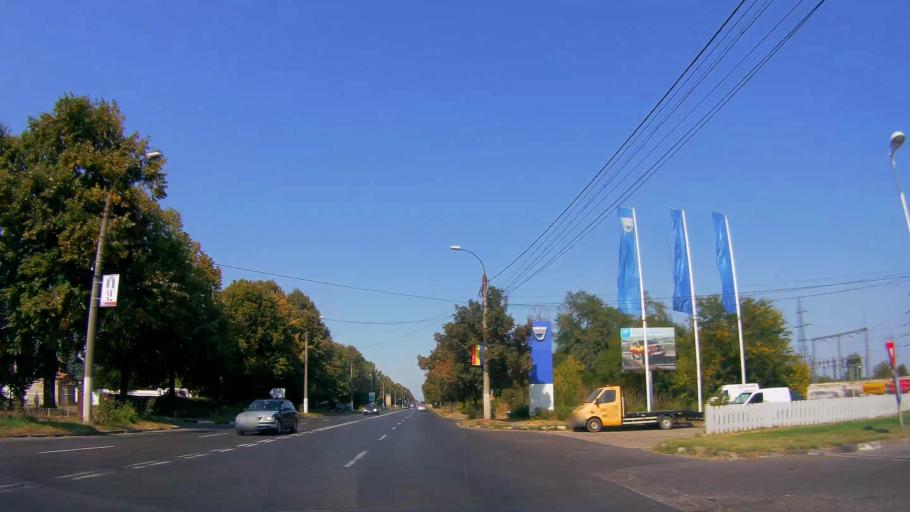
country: RO
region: Giurgiu
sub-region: Comuna Fratesti
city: Remus
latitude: 43.9190
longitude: 25.9729
